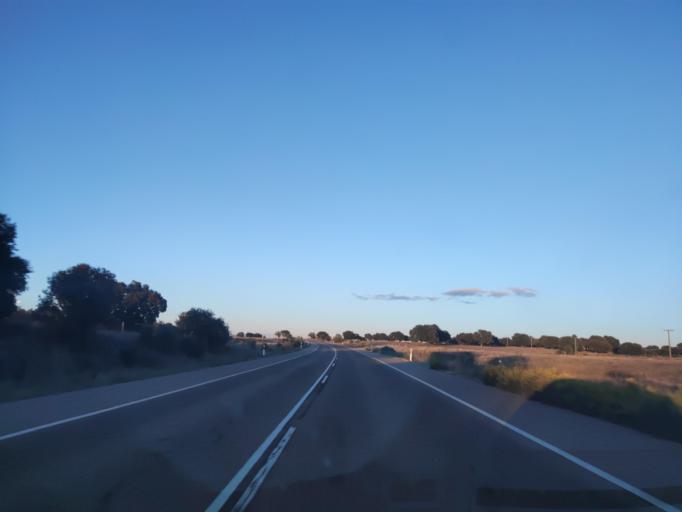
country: ES
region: Castille and Leon
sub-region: Provincia de Salamanca
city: Martin de Yeltes
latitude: 40.7801
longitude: -6.2690
